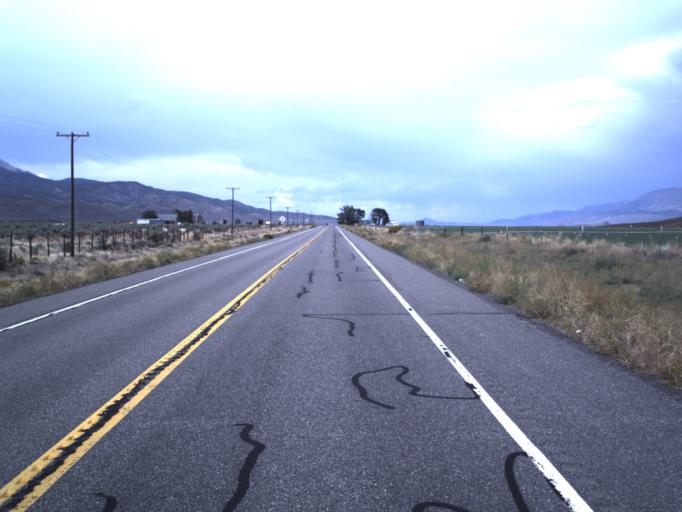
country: US
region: Utah
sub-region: Piute County
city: Junction
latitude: 38.2477
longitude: -112.2202
